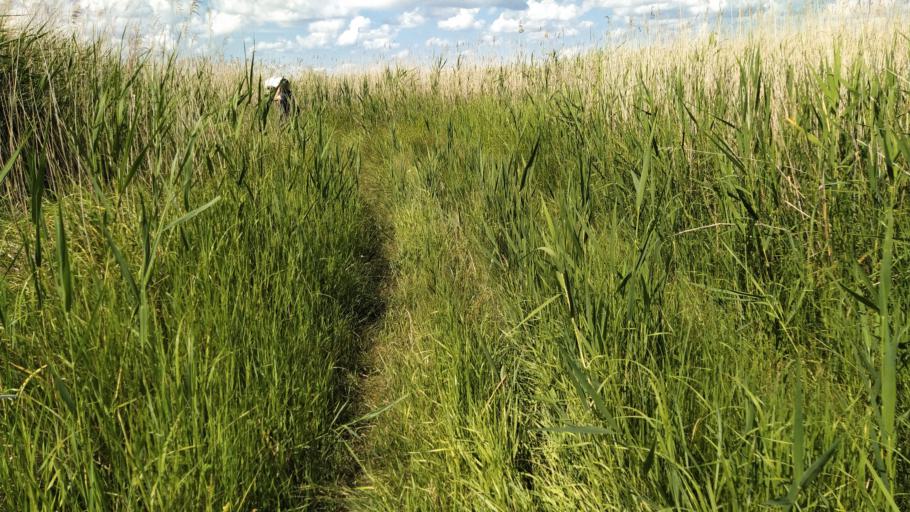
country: RU
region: Rostov
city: Bataysk
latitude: 47.1377
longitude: 39.6694
